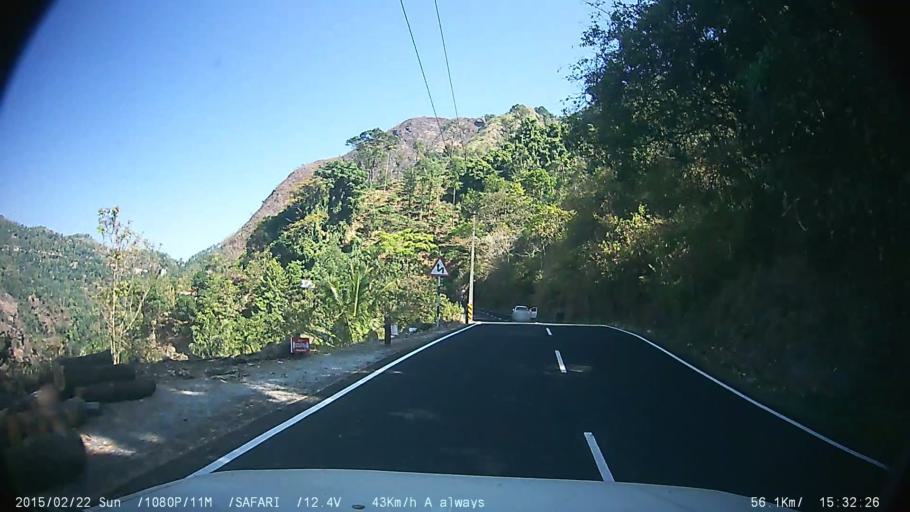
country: IN
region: Kerala
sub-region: Kottayam
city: Erattupetta
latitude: 9.5569
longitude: 76.9613
